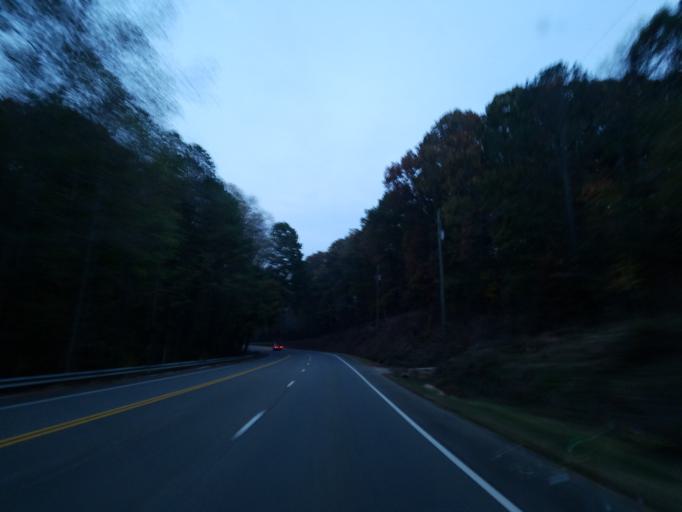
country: US
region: Georgia
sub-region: Pickens County
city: Jasper
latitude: 34.5034
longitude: -84.4860
